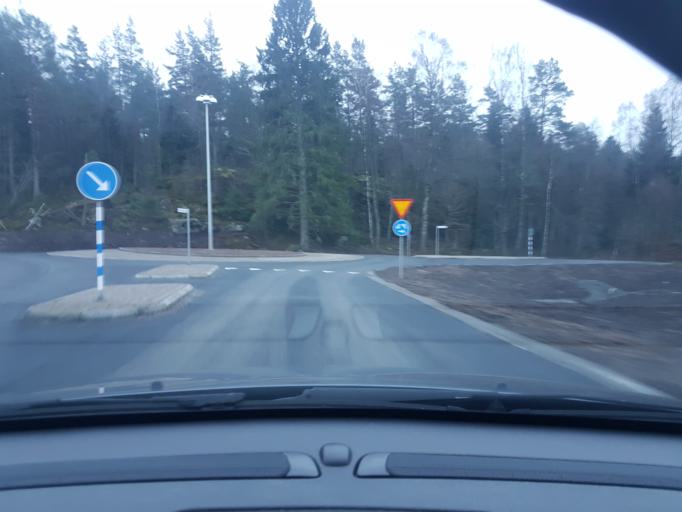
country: SE
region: Vaestra Goetaland
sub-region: Ale Kommun
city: Alvangen
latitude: 57.9458
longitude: 12.1226
